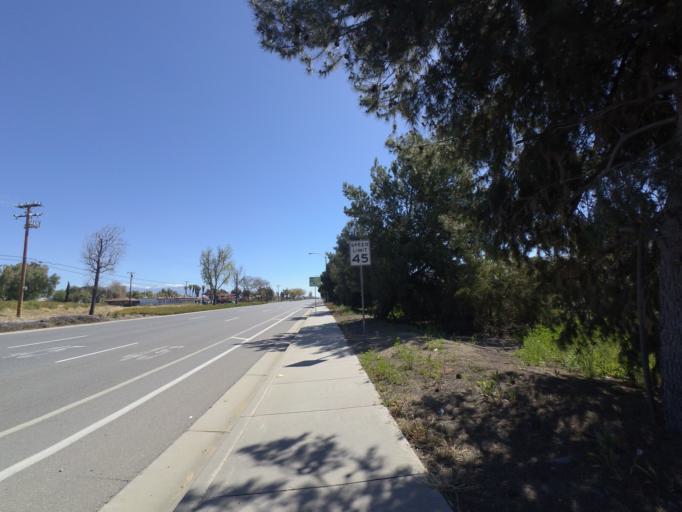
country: US
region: California
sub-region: Riverside County
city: March Air Force Base
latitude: 33.9167
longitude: -117.2780
